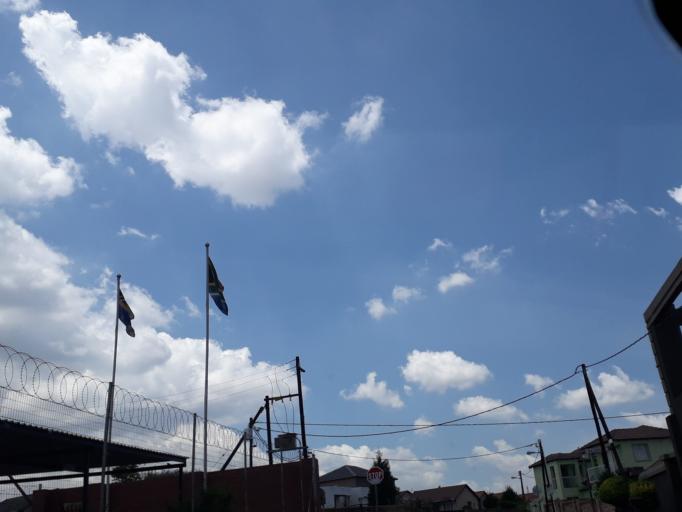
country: ZA
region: Gauteng
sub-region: West Rand District Municipality
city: Muldersdriseloop
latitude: -26.0379
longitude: 27.9213
